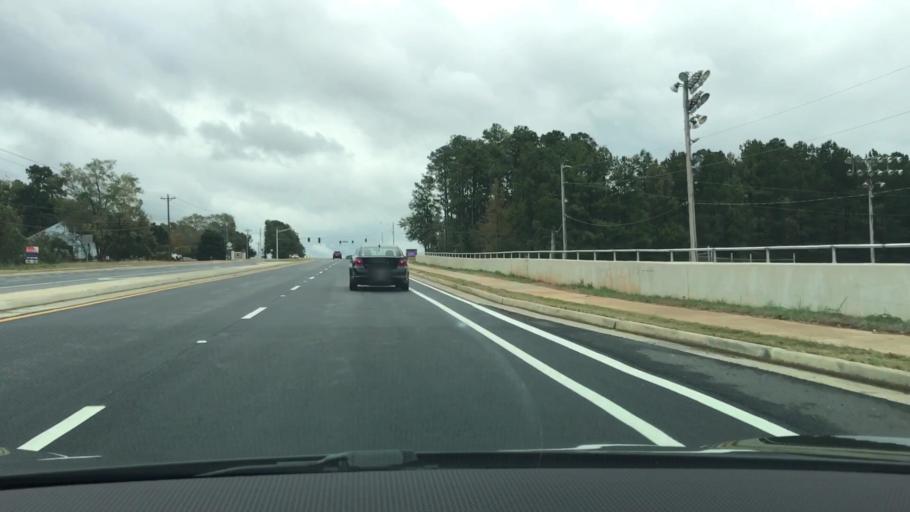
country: US
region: Georgia
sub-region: Oconee County
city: Watkinsville
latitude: 33.8763
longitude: -83.4472
